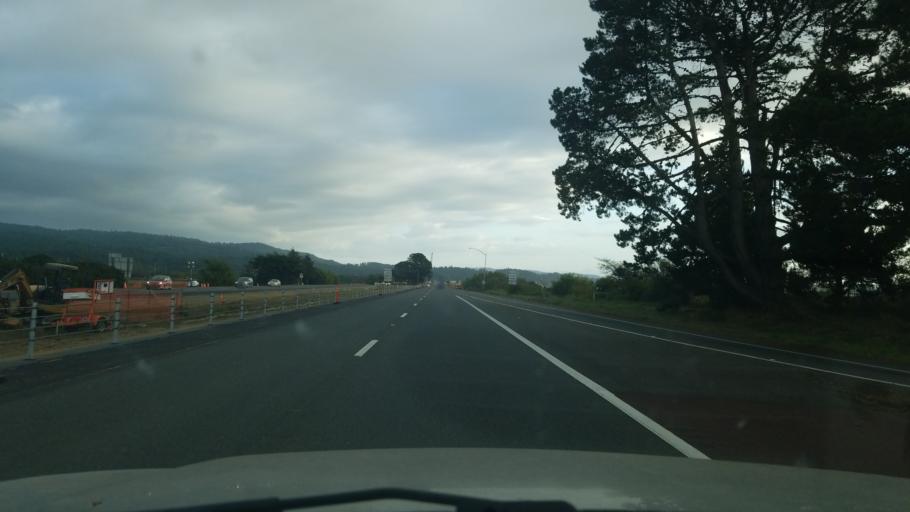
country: US
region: California
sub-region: Humboldt County
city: Arcata
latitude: 40.8506
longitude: -124.0821
